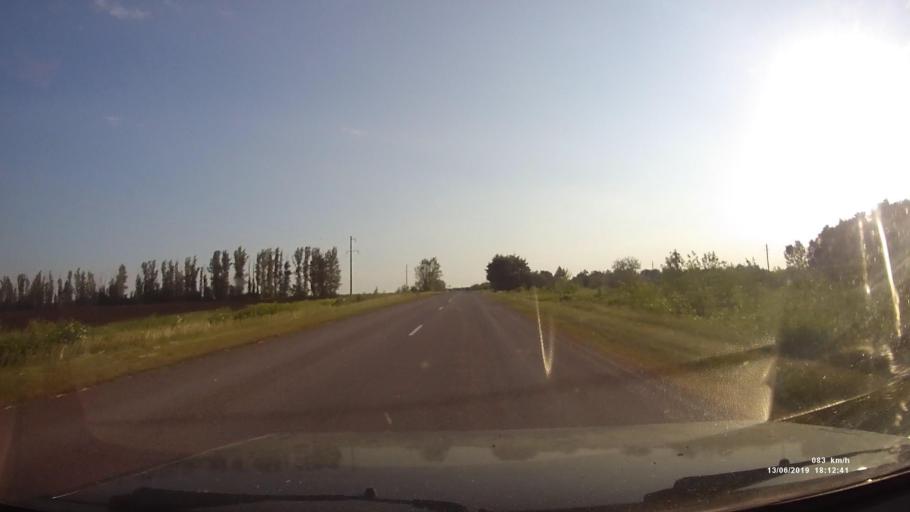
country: RU
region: Rostov
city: Kazanskaya
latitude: 49.9438
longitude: 41.4067
